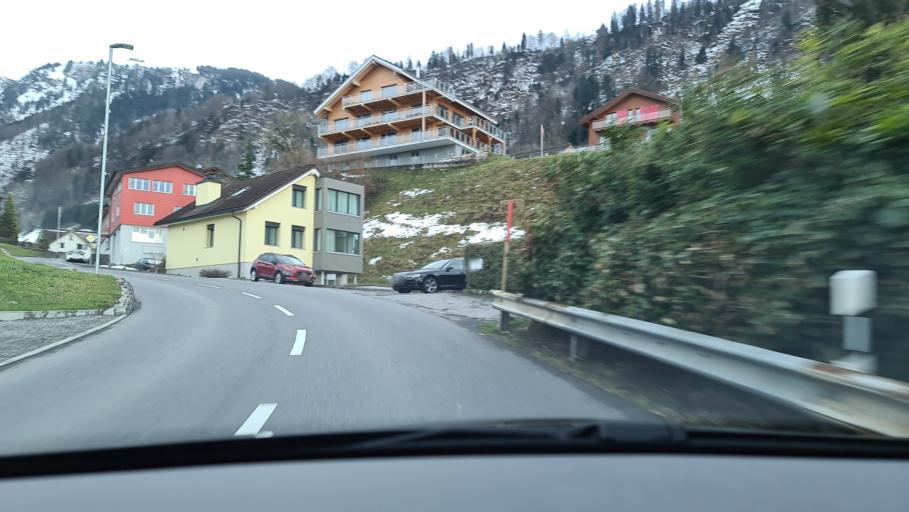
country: CH
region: Nidwalden
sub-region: Nidwalden
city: Emmetten
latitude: 46.9580
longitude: 8.5094
